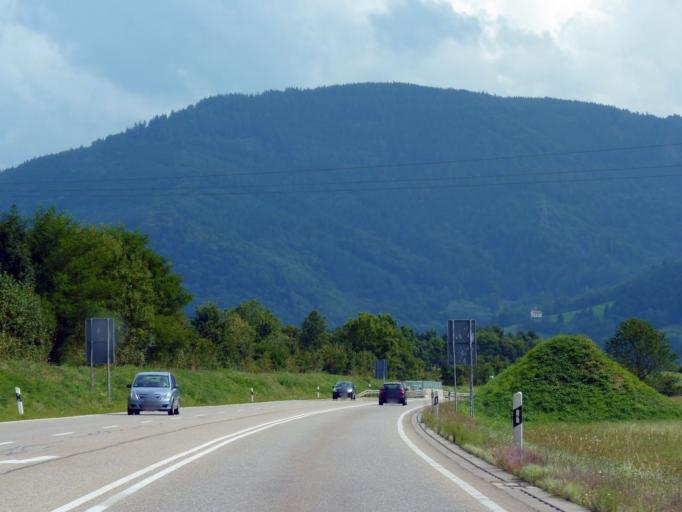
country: DE
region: Baden-Wuerttemberg
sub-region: Freiburg Region
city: Stegen
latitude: 47.9707
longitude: 7.9711
